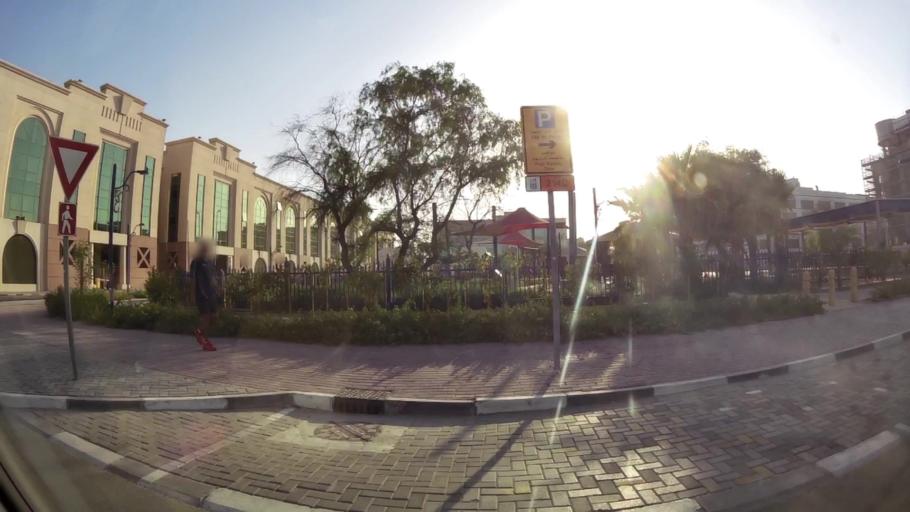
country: AE
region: Ash Shariqah
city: Sharjah
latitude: 25.2460
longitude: 55.3428
